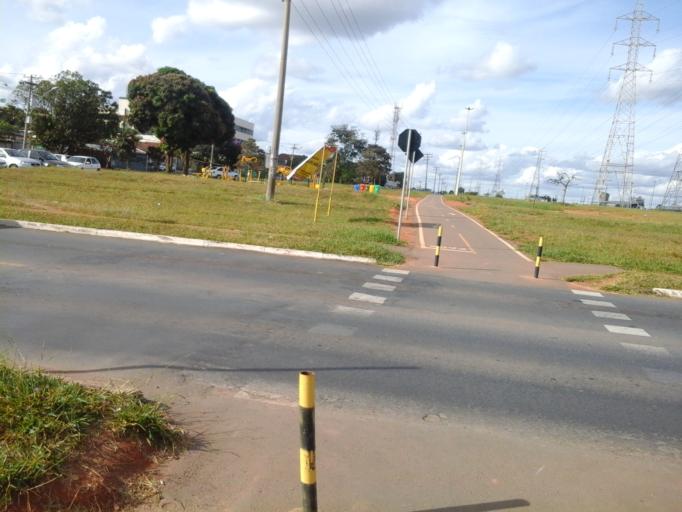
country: BR
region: Federal District
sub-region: Brasilia
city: Brasilia
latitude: -15.8270
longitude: -47.9868
